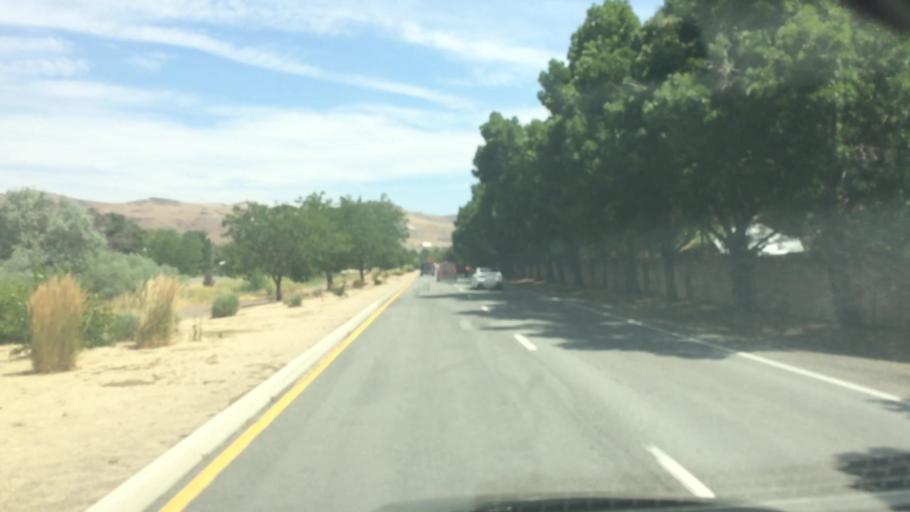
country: US
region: Nevada
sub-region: Washoe County
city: Sparks
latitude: 39.5529
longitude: -119.7215
